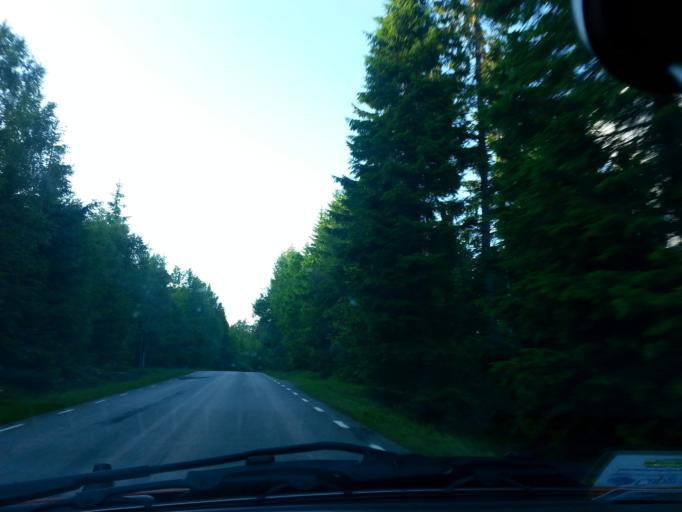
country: SE
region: Joenkoeping
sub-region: Gislaveds Kommun
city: Reftele
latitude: 57.2347
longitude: 13.6440
